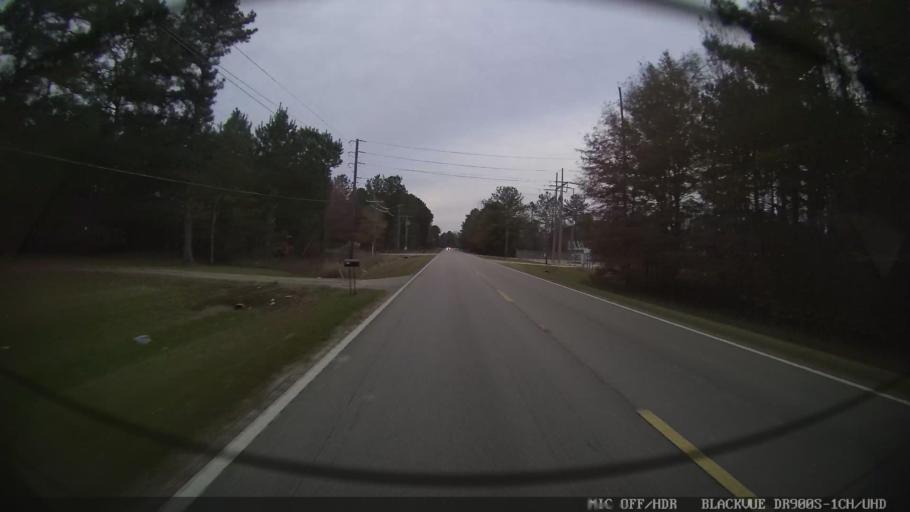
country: US
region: Mississippi
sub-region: Clarke County
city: Stonewall
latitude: 32.0261
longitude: -88.8584
